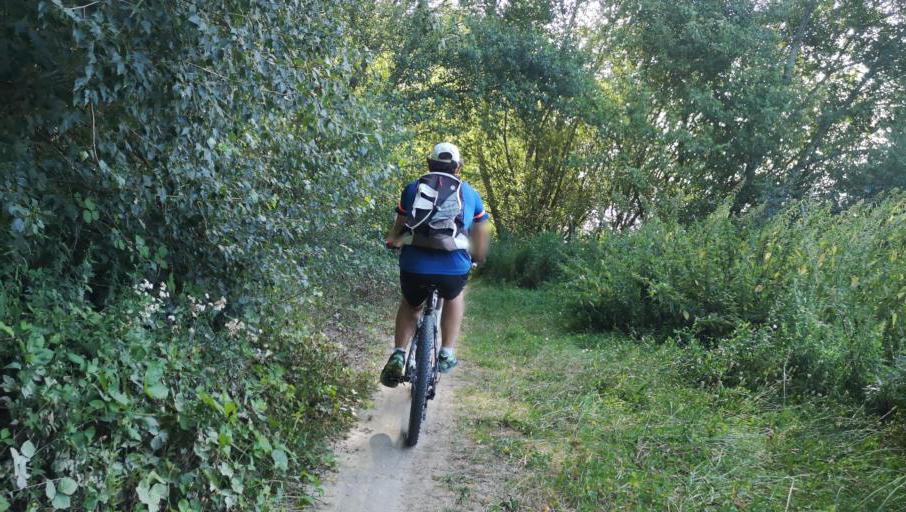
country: FR
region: Centre
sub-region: Departement du Loiret
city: Darvoy
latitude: 47.8736
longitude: 2.1061
